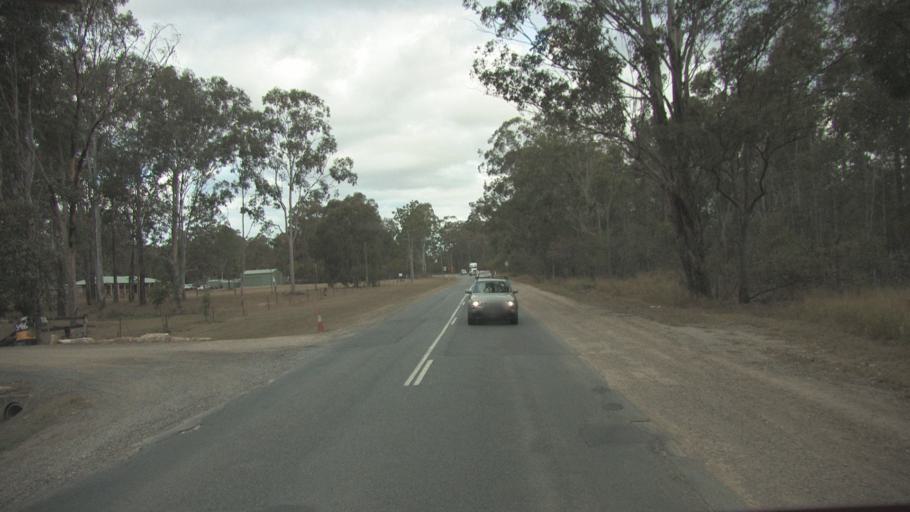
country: AU
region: Queensland
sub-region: Logan
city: Cedar Vale
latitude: -27.8598
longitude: 153.0554
